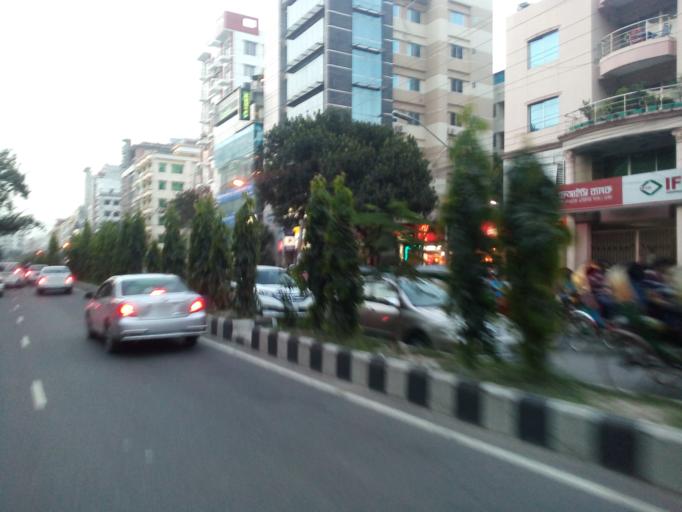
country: BD
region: Dhaka
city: Tungi
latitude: 23.8757
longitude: 90.3908
